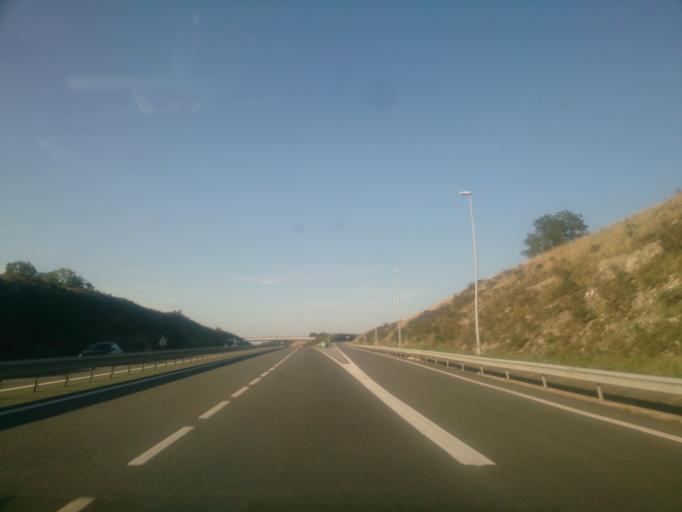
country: FR
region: Midi-Pyrenees
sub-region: Departement du Lot
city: Le Vigan
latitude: 44.6574
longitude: 1.5656
